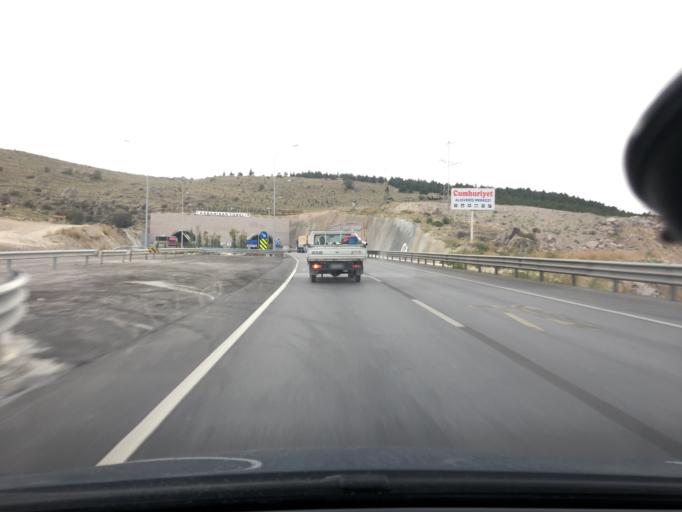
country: TR
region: Afyonkarahisar
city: Afyonkarahisar
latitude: 38.7951
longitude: 30.4391
